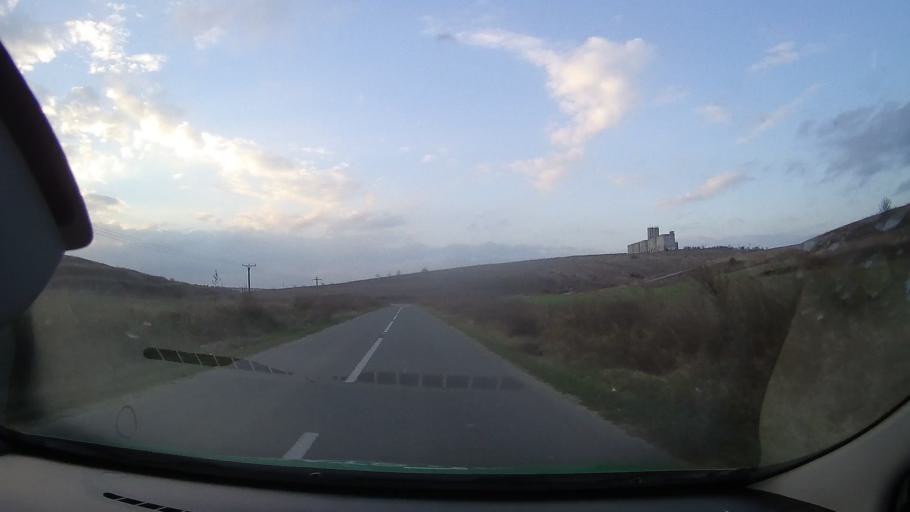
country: RO
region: Constanta
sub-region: Comuna Baneasa
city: Baneasa
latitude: 44.0584
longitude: 27.7185
